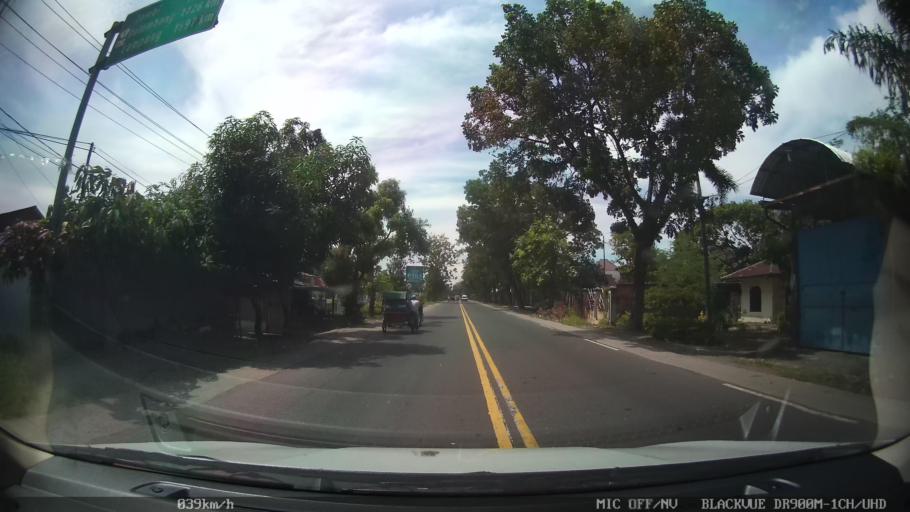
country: ID
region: North Sumatra
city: Binjai
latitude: 3.6399
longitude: 98.5104
